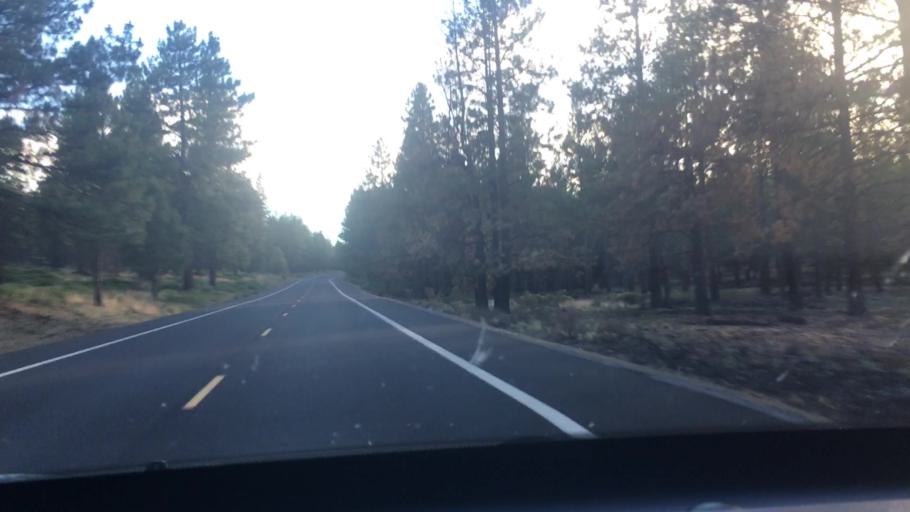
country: US
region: Oregon
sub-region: Deschutes County
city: Deschutes River Woods
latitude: 44.0473
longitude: -121.3956
